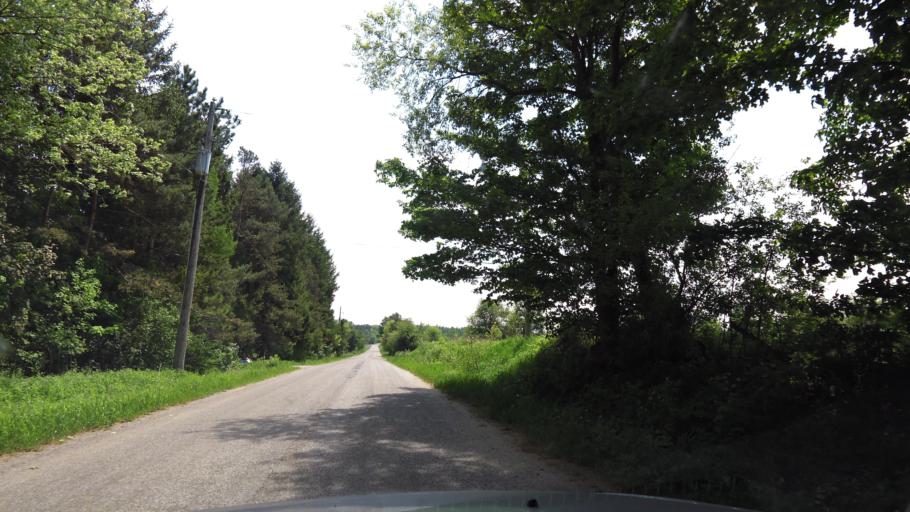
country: CA
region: Ontario
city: Cobourg
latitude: 43.9854
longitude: -78.4799
